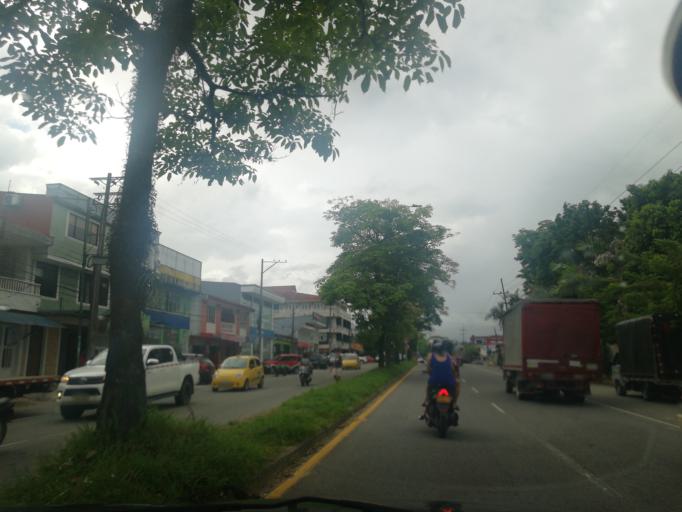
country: CO
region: Meta
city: Acacias
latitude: 3.9874
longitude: -73.7661
